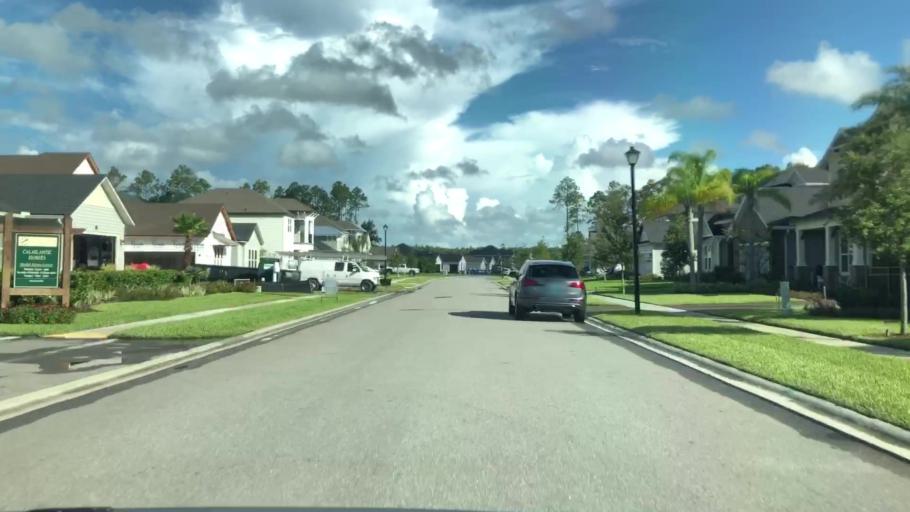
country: US
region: Florida
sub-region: Saint Johns County
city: Palm Valley
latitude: 30.1346
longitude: -81.4098
